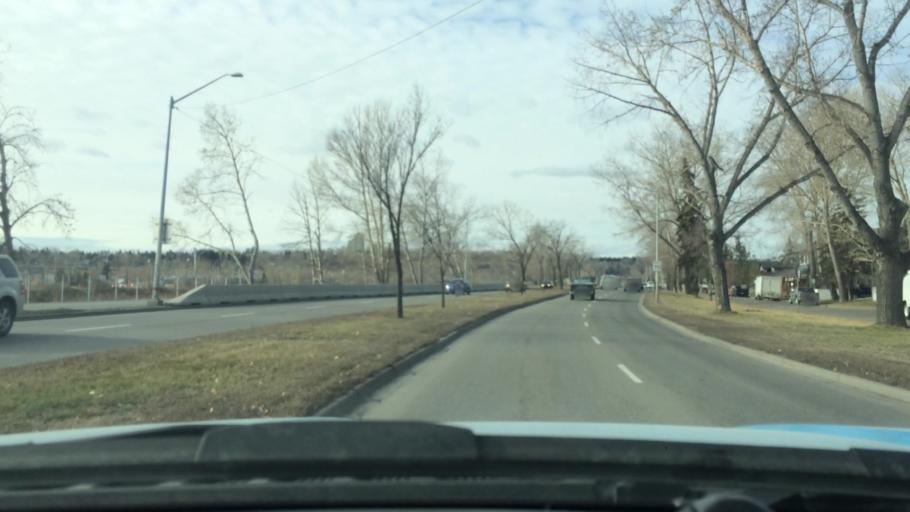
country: CA
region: Alberta
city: Calgary
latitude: 51.0489
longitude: -114.0995
